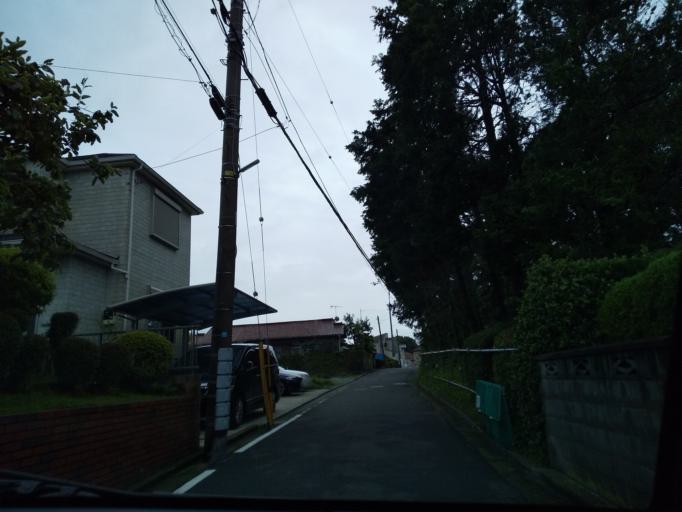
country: JP
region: Kanagawa
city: Fujisawa
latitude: 35.3944
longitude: 139.5138
